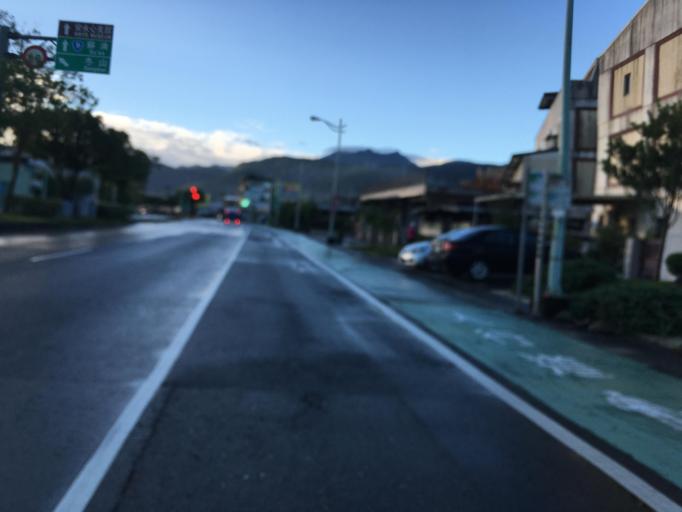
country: TW
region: Taiwan
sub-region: Yilan
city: Yilan
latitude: 24.6374
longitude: 121.7870
